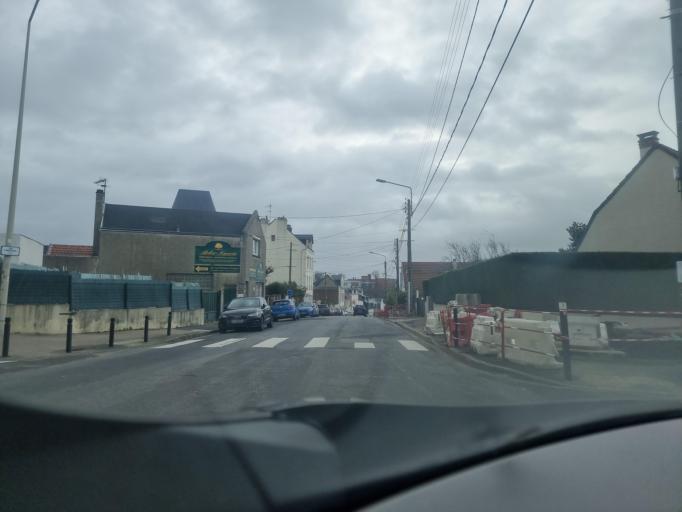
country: FR
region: Haute-Normandie
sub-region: Departement de la Seine-Maritime
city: Le Havre
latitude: 49.5039
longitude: 0.1018
